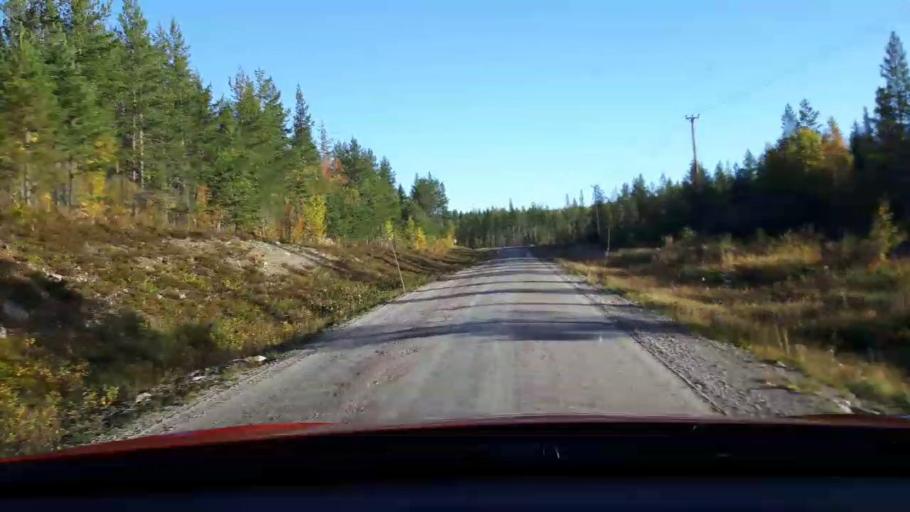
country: SE
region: Jaemtland
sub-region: Stroemsunds Kommun
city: Stroemsund
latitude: 64.3846
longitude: 15.1506
